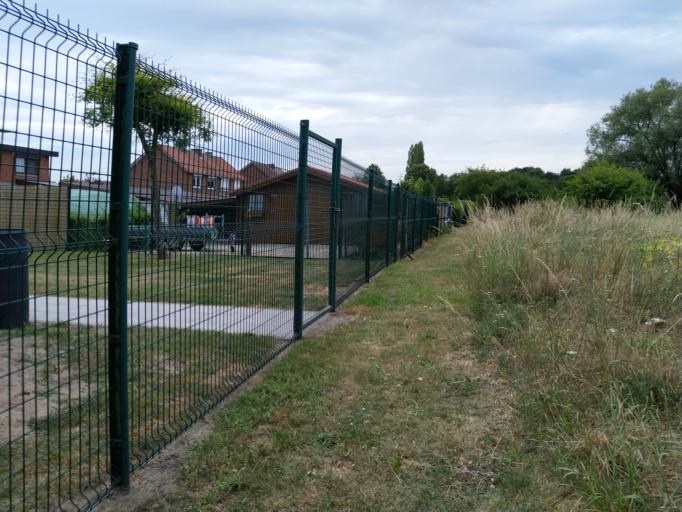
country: BE
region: Wallonia
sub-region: Province du Hainaut
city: Mons
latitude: 50.4872
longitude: 3.9559
